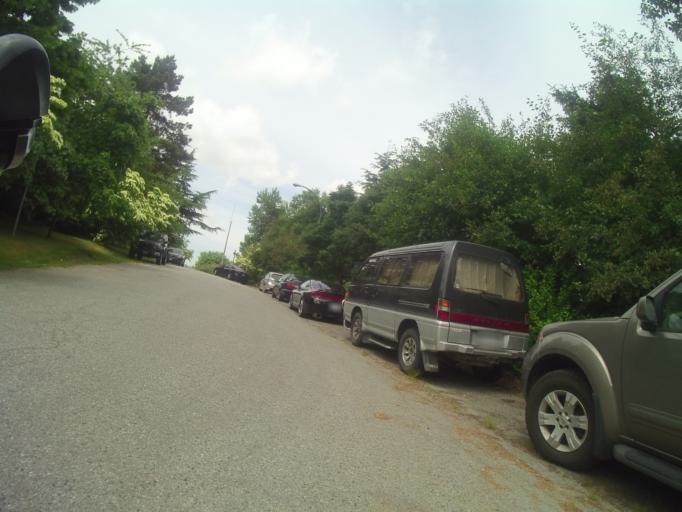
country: CA
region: British Columbia
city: Vancouver
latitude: 49.2647
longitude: -123.0755
